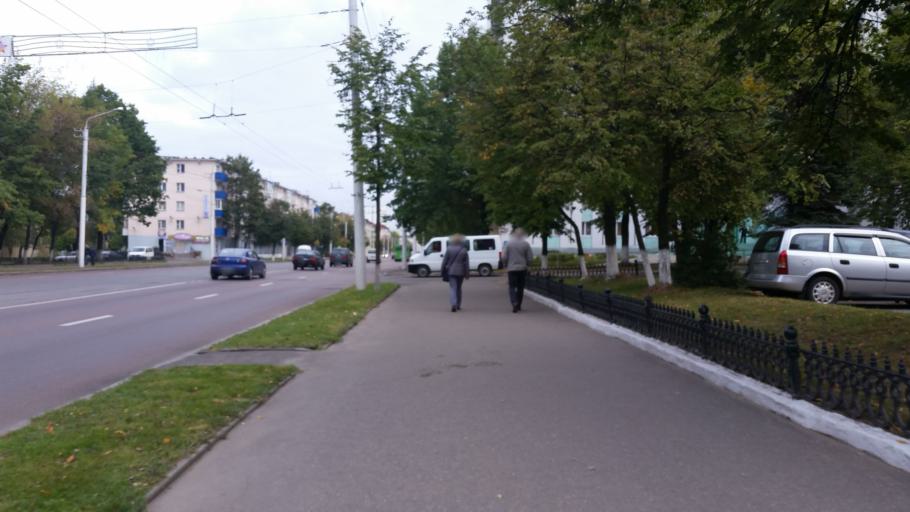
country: BY
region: Vitebsk
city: Vitebsk
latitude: 55.1752
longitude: 30.2003
